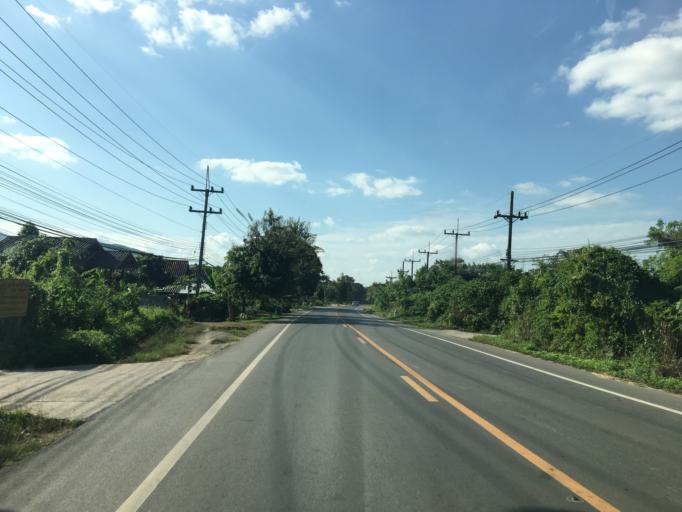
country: TH
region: Phayao
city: Chun
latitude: 19.3448
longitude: 100.1181
